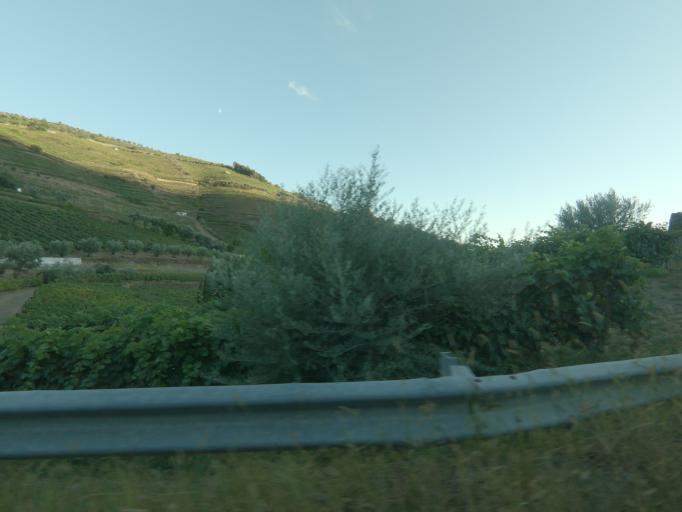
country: PT
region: Vila Real
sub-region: Mesao Frio
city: Mesao Frio
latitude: 41.1773
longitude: -7.8517
